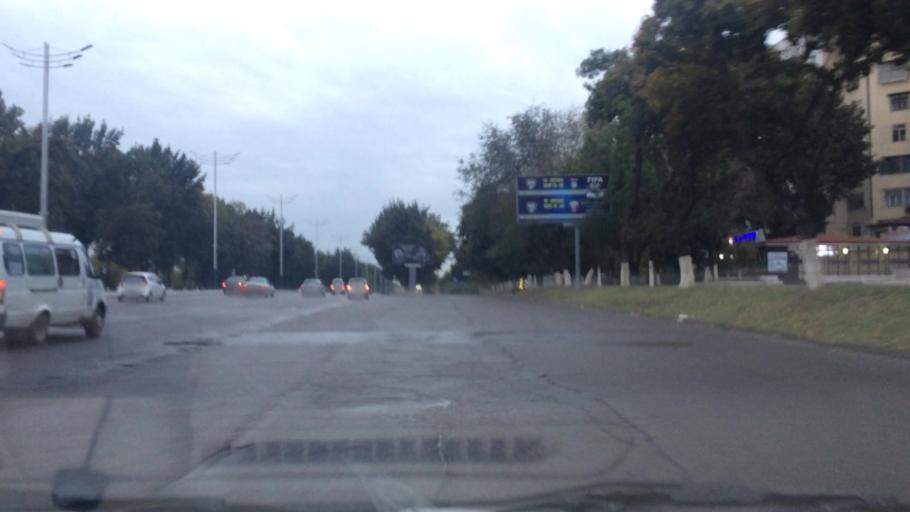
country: UZ
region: Toshkent Shahri
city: Tashkent
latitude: 41.3080
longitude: 69.2380
